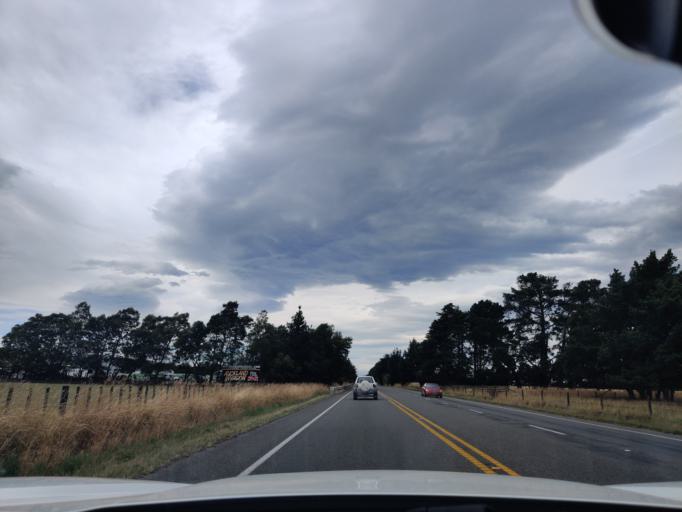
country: NZ
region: Wellington
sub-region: Masterton District
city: Masterton
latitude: -40.9771
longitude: 175.5912
